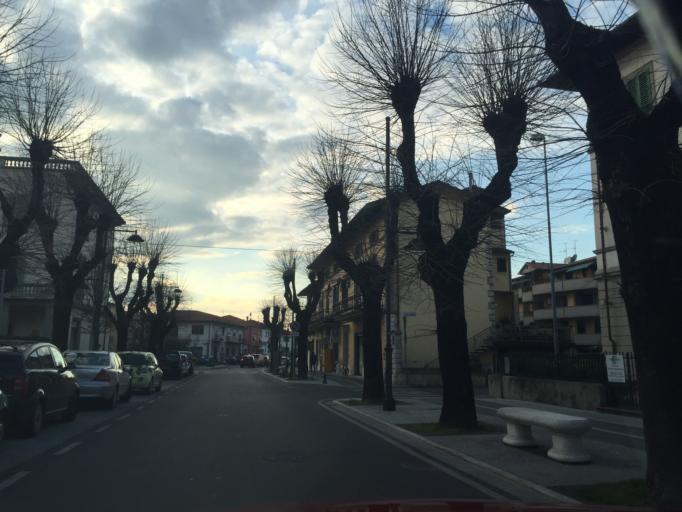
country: IT
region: Tuscany
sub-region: Provincia di Pistoia
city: Monsummano Terme
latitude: 43.8714
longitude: 10.8123
